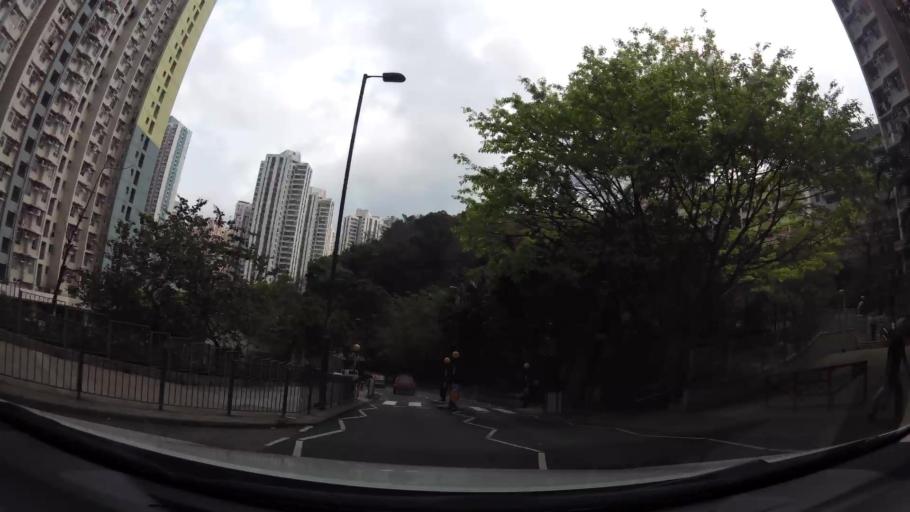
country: HK
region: Kowloon City
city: Kowloon
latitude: 22.3196
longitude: 114.2165
